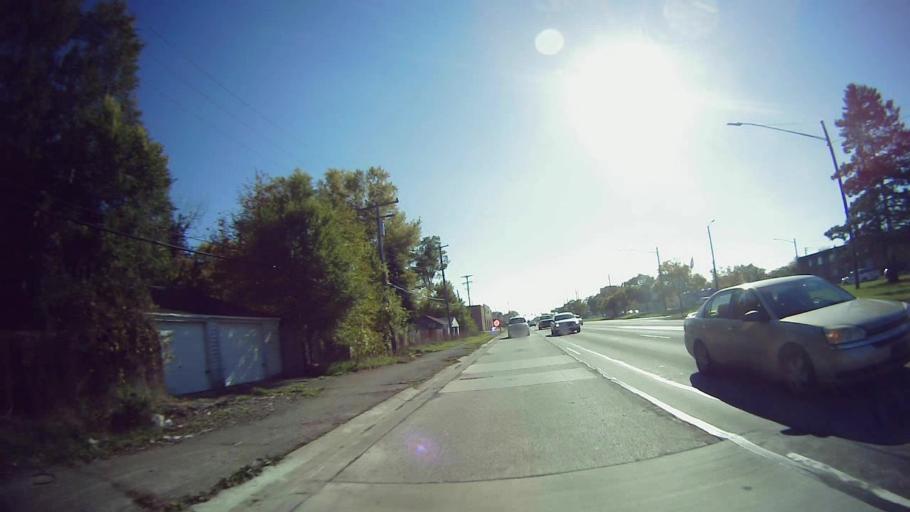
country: US
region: Michigan
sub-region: Wayne County
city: Redford
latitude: 42.4264
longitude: -83.2773
